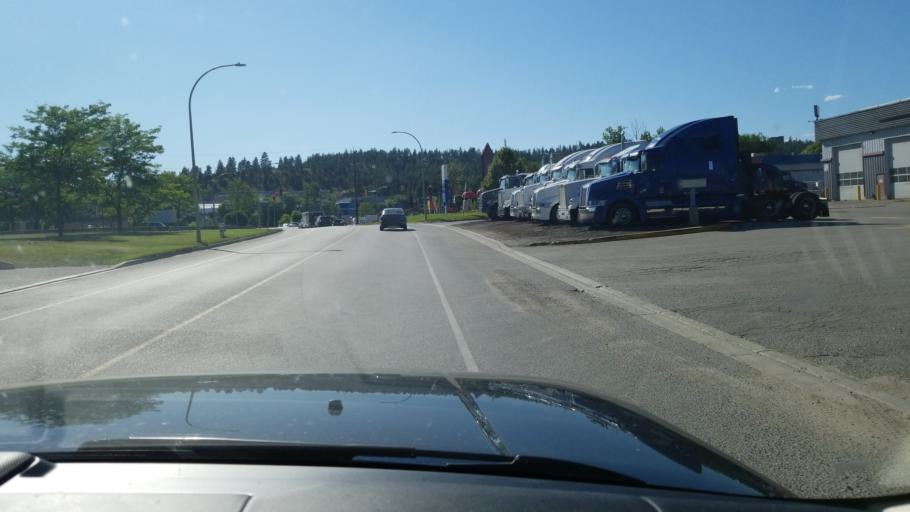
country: CA
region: British Columbia
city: Kelowna
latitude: 49.9243
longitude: -119.3846
